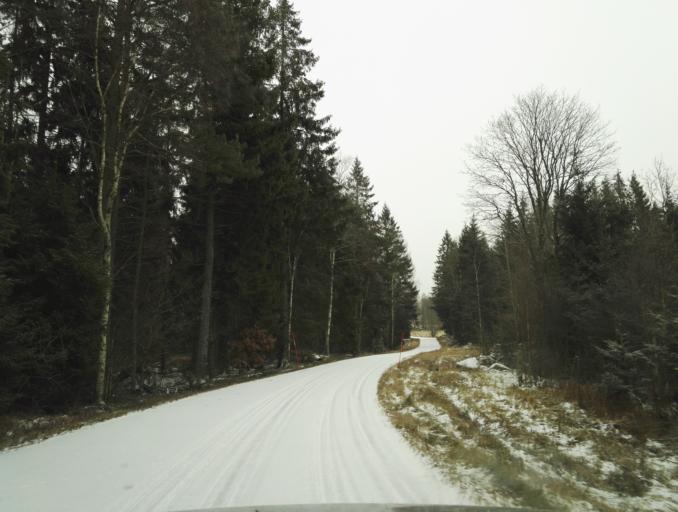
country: SE
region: Kronoberg
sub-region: Alvesta Kommun
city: Vislanda
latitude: 56.6823
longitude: 14.4345
